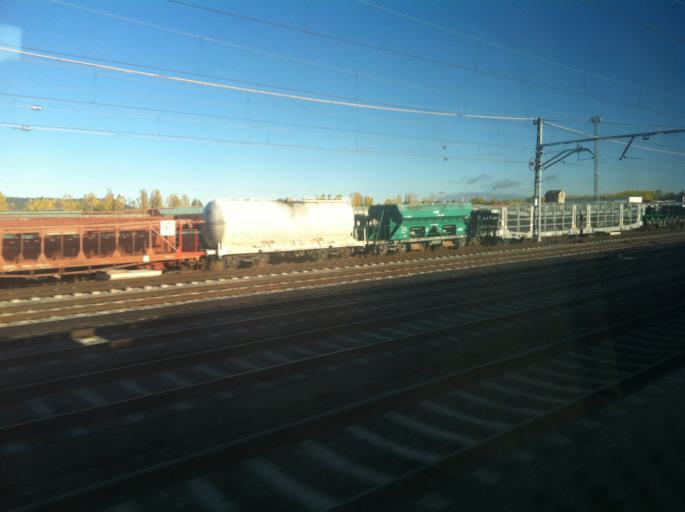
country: ES
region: Castille and Leon
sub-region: Provincia de Palencia
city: Venta de Banos
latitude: 41.9105
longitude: -4.5044
